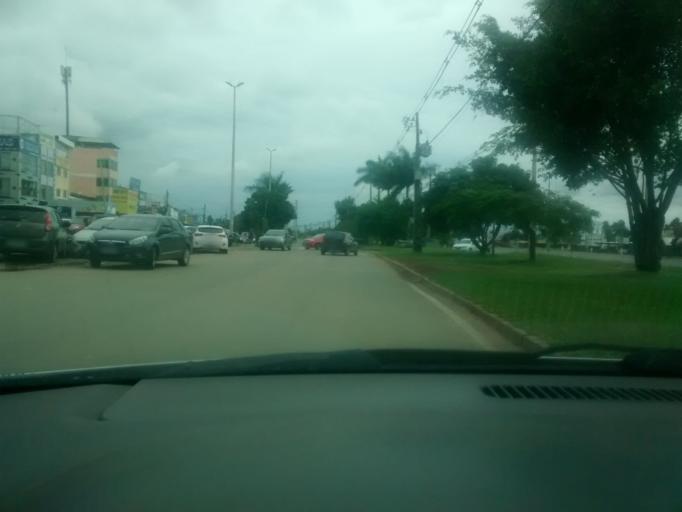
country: BR
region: Federal District
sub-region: Brasilia
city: Brasilia
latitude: -15.8716
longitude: -47.8223
